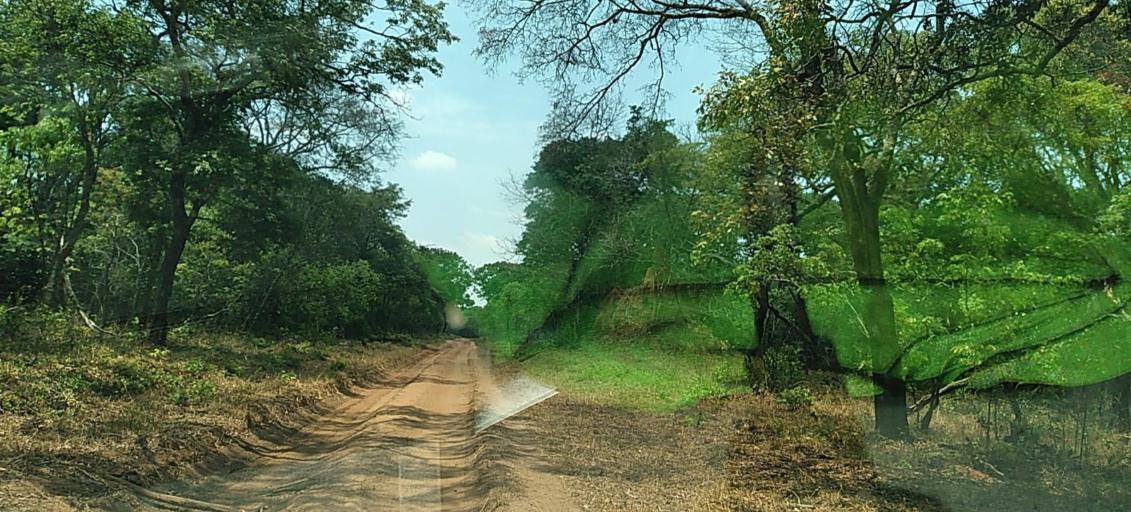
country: CD
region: Katanga
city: Kolwezi
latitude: -11.3522
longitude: 25.2125
